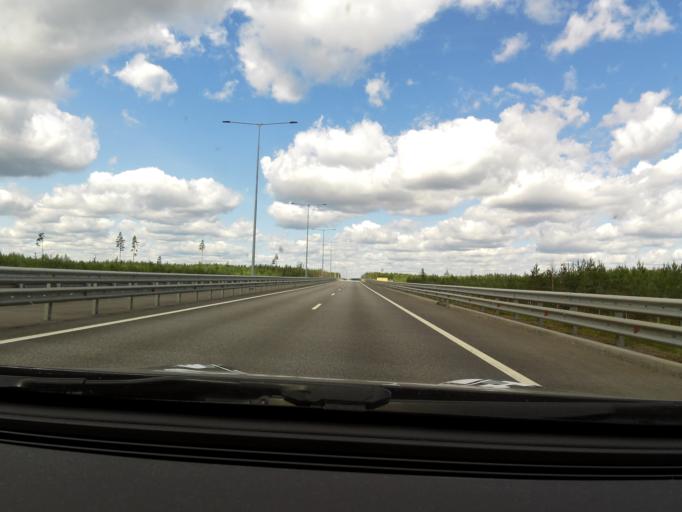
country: RU
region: Tverskaya
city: Krasnomayskiy
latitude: 57.4371
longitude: 34.4537
